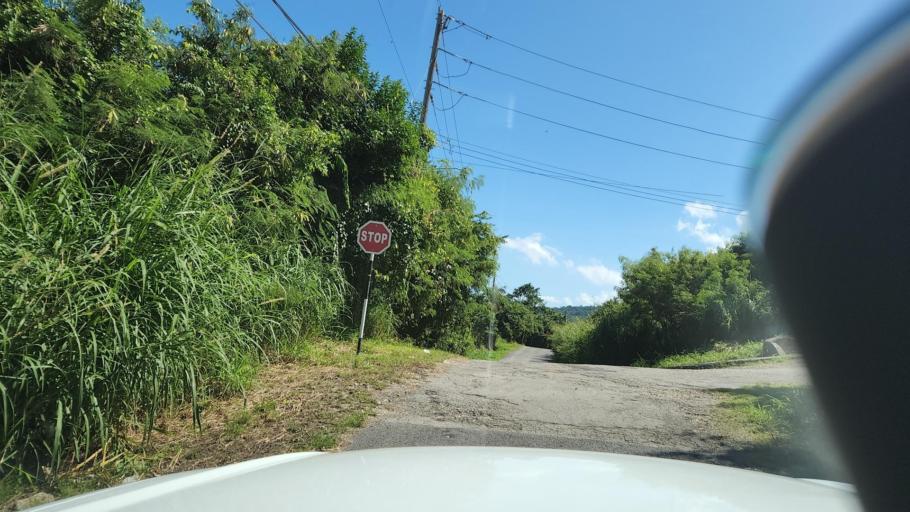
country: BB
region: Saint Joseph
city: Bathsheba
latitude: 13.2173
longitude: -59.5417
